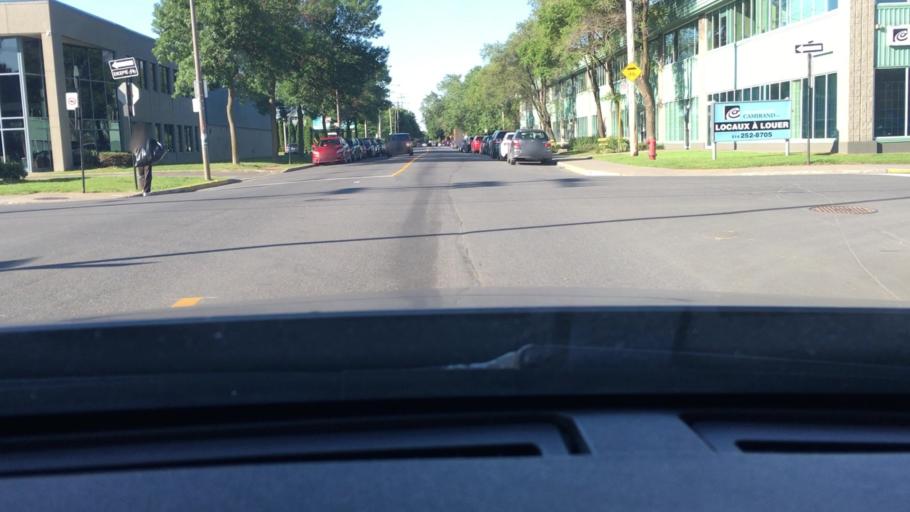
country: CA
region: Quebec
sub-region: Monteregie
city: Longueuil
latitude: 45.5562
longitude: -73.5418
